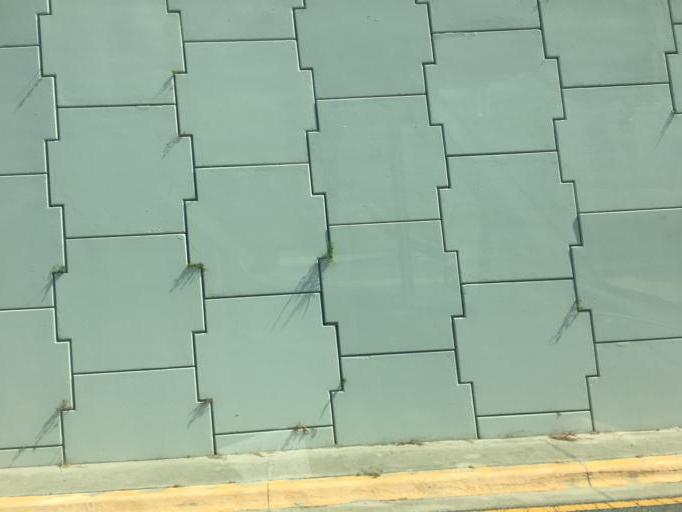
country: US
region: Florida
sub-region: Bay County
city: Upper Grand Lagoon
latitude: 30.1877
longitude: -85.7643
